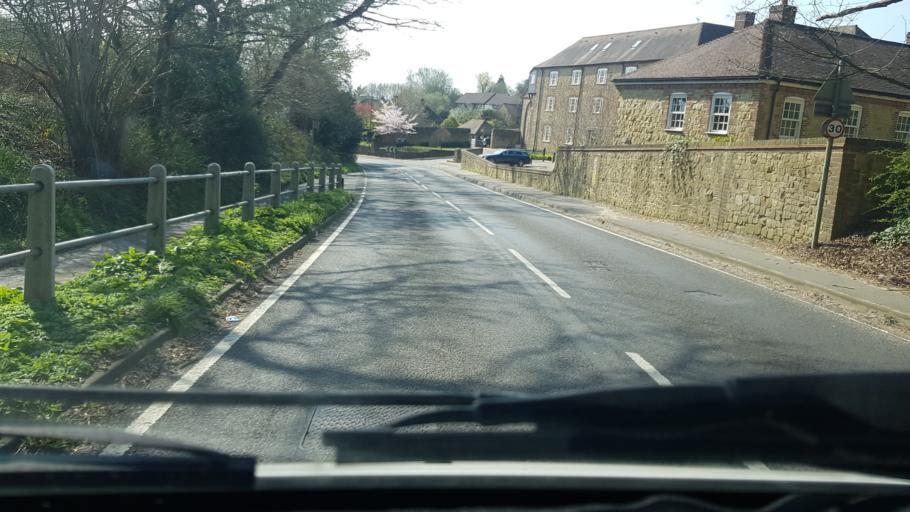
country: GB
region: England
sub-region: West Sussex
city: Midhurst
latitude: 51.0019
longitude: -0.7312
